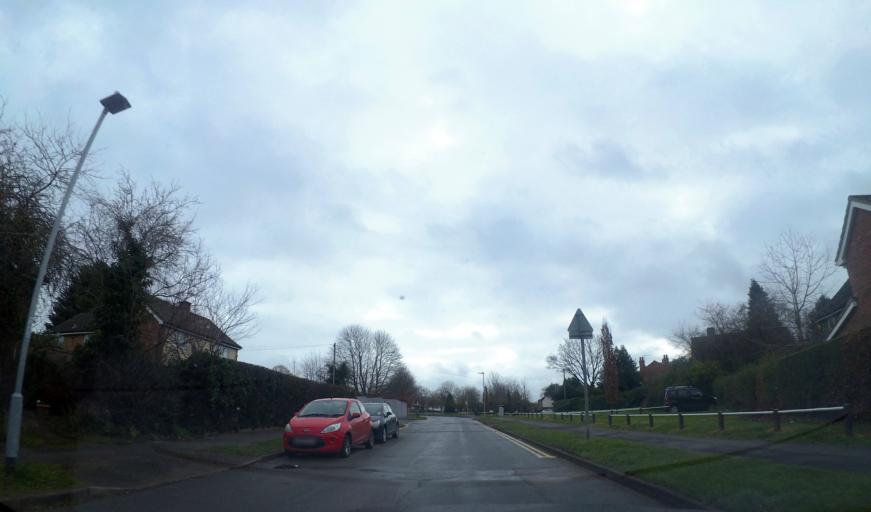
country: GB
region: England
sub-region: West Berkshire
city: Tilehurst
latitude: 51.4418
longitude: -1.0211
